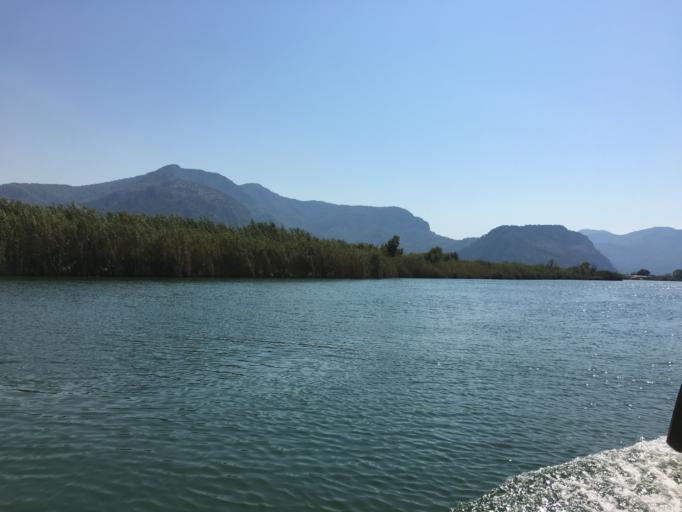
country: TR
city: Dalyan
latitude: 36.8234
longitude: 28.6342
